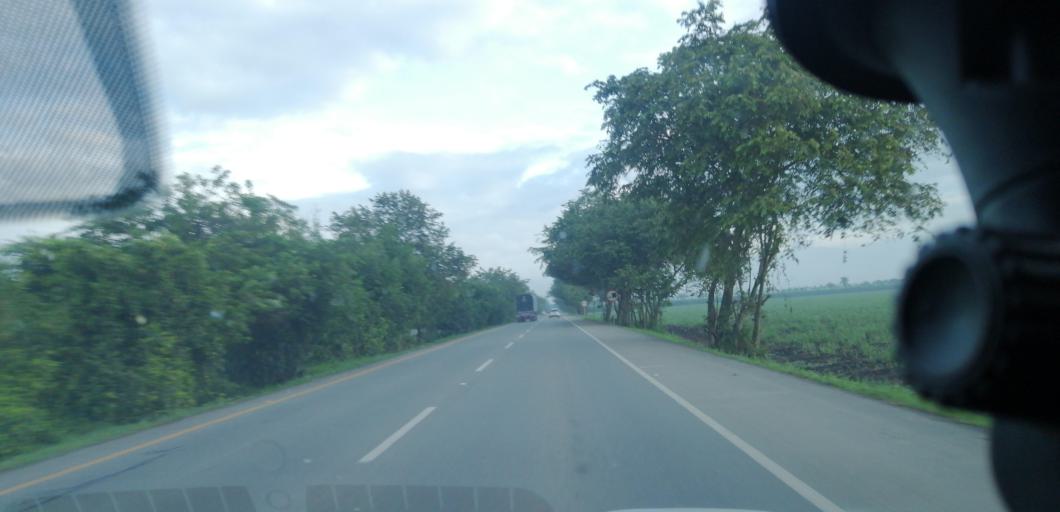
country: CO
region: Valle del Cauca
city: Palmira
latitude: 3.5498
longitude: -76.3380
